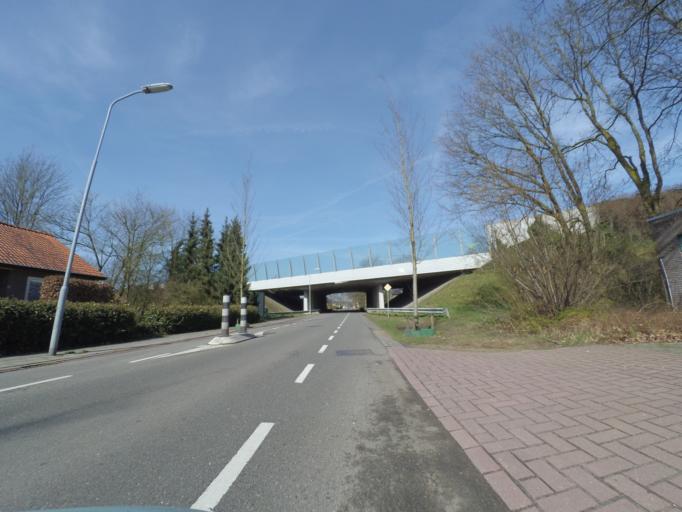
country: NL
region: Gelderland
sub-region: Gemeente Barneveld
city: Stroe
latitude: 52.1893
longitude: 5.6892
